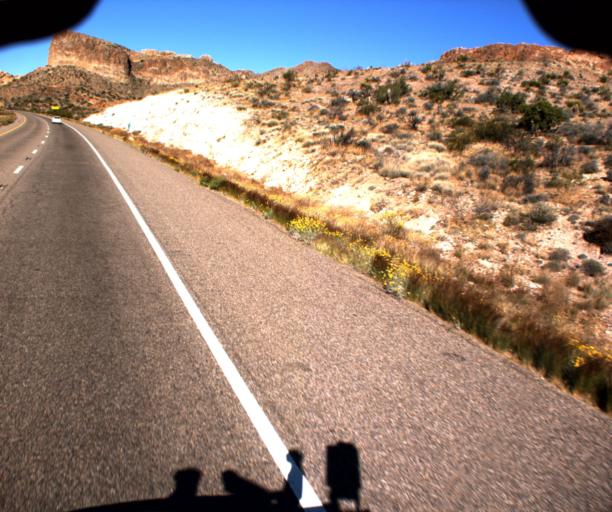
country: US
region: Arizona
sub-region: Mohave County
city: Golden Valley
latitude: 35.2286
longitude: -114.3738
